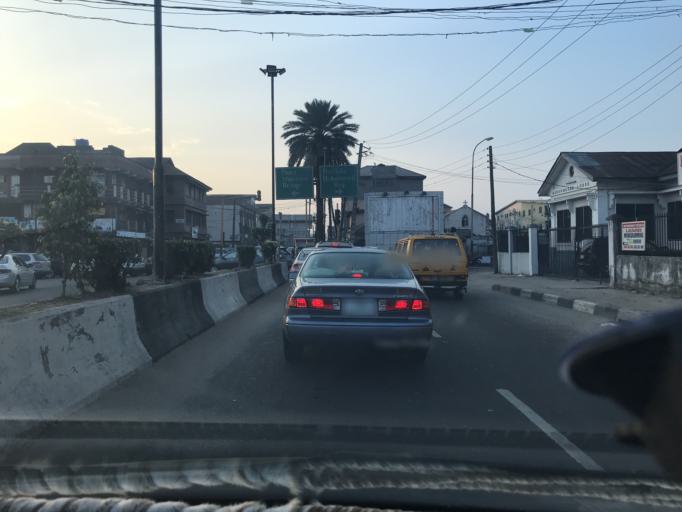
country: NG
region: Lagos
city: Makoko
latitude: 6.4916
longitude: 3.3821
